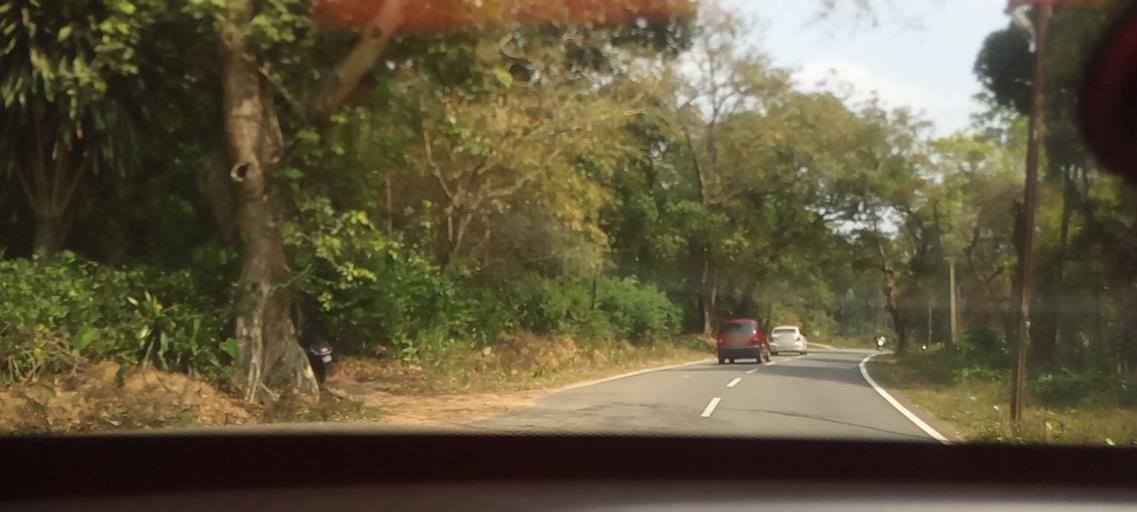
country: IN
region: Karnataka
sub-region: Chikmagalur
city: Chikmagalur
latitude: 13.2622
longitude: 75.6715
